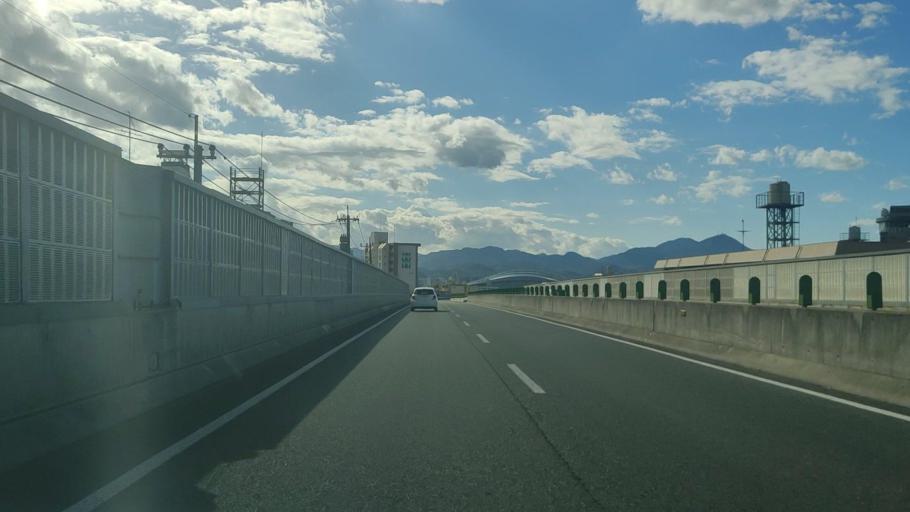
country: JP
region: Yamaguchi
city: Shimonoseki
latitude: 33.8815
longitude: 130.9045
